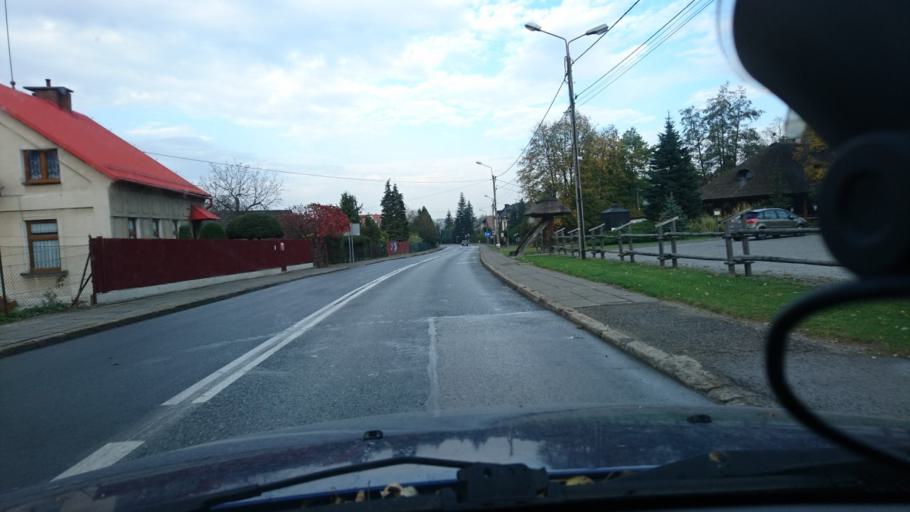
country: PL
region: Silesian Voivodeship
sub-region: Powiat bielski
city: Wilkowice
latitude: 49.7984
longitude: 19.0923
